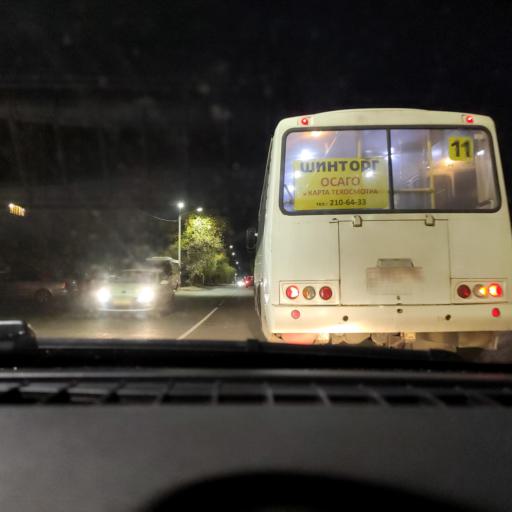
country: RU
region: Voronezj
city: Maslovka
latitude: 51.5935
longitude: 39.2437
